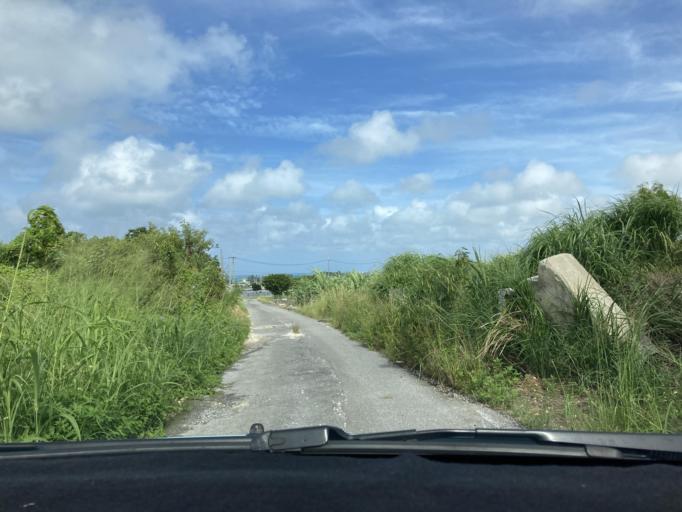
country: JP
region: Okinawa
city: Itoman
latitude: 26.0962
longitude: 127.6666
